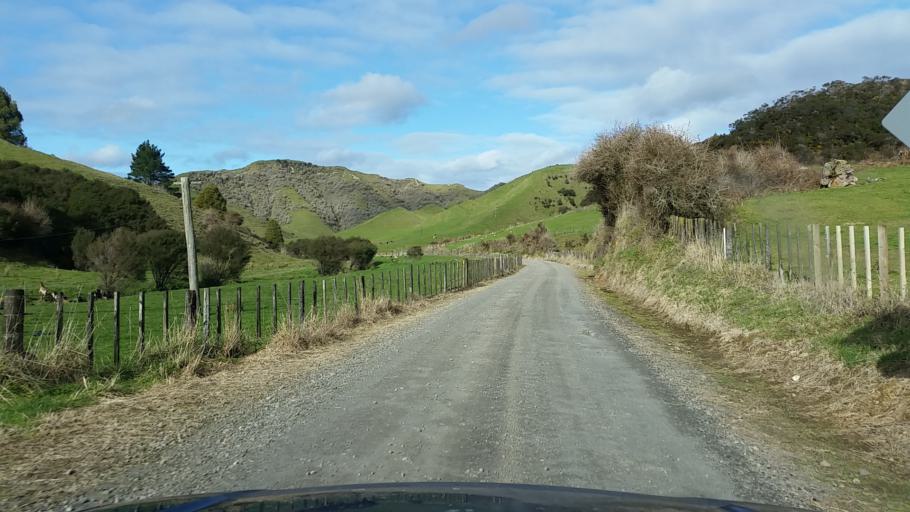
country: NZ
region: Taranaki
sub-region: South Taranaki District
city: Eltham
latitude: -39.2595
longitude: 174.5767
